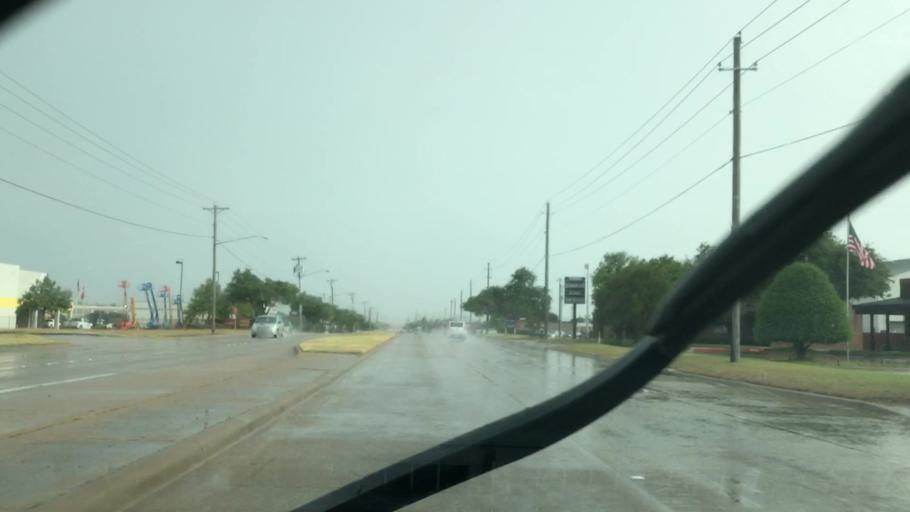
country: US
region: Texas
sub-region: Dallas County
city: Richardson
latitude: 32.8995
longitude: -96.7006
